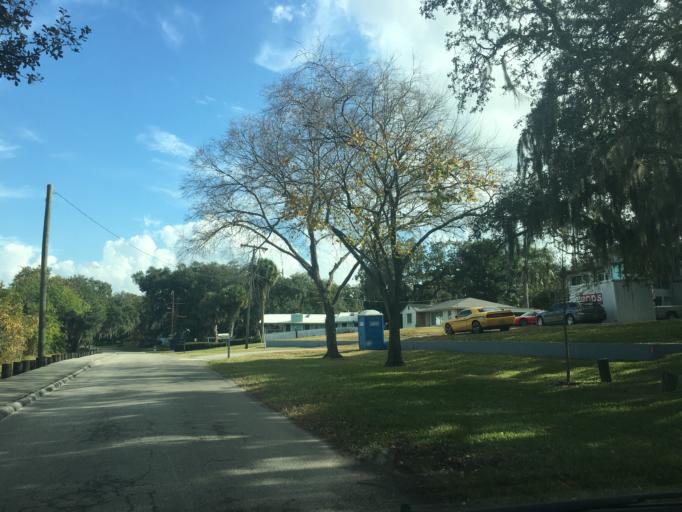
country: US
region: Florida
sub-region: Hillsborough County
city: Egypt Lake-Leto
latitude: 27.9982
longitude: -82.4731
